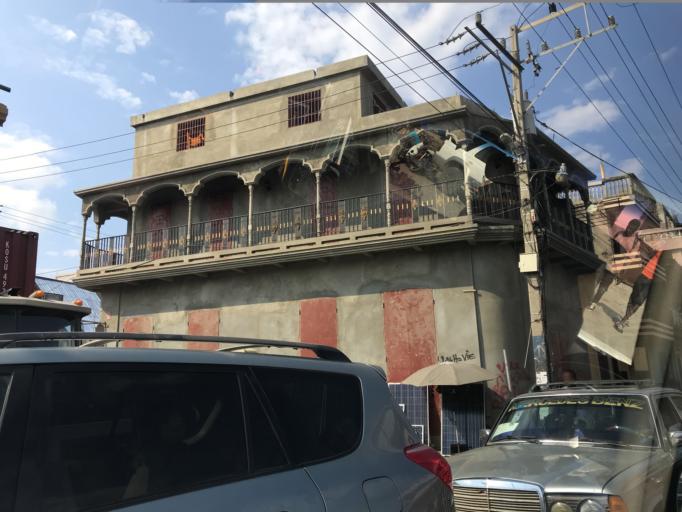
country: HT
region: Nord
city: Okap
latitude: 19.7542
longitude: -72.2031
